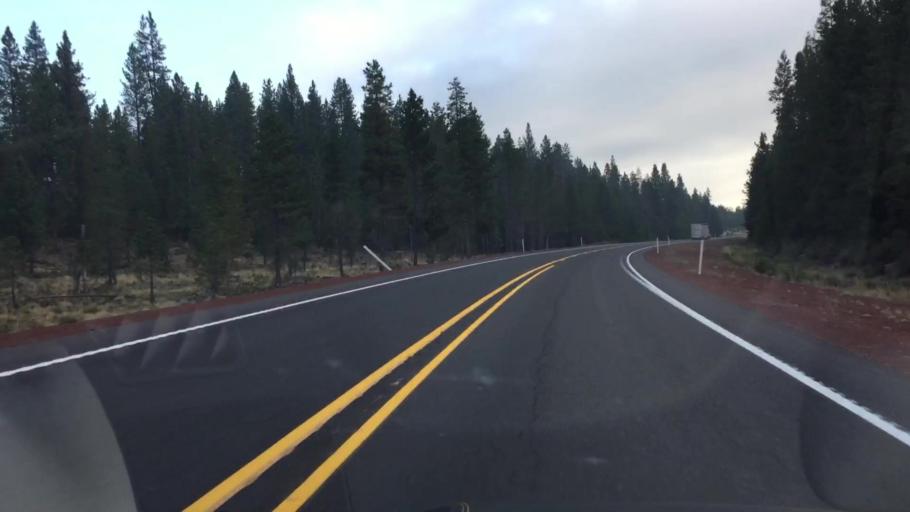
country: US
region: Oregon
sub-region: Deschutes County
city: La Pine
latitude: 43.3126
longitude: -121.7677
